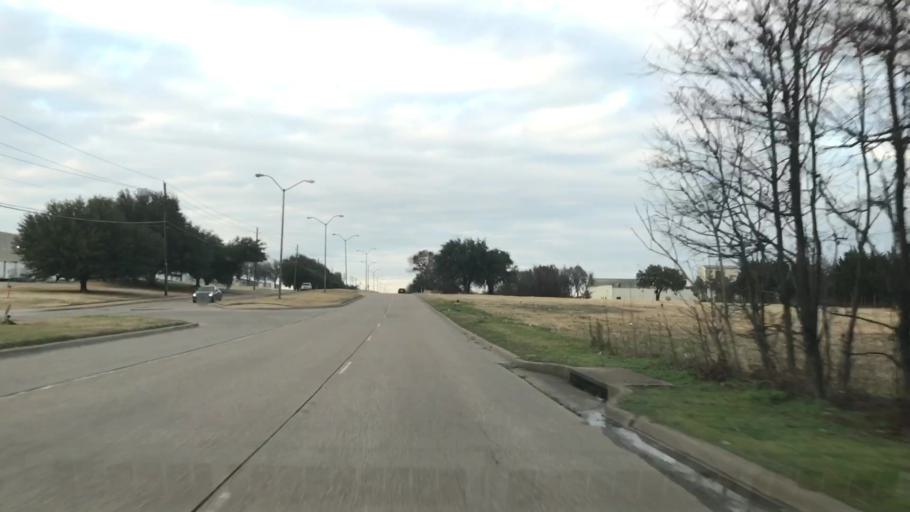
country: US
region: Texas
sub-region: Dallas County
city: Duncanville
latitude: 32.6953
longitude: -96.9085
